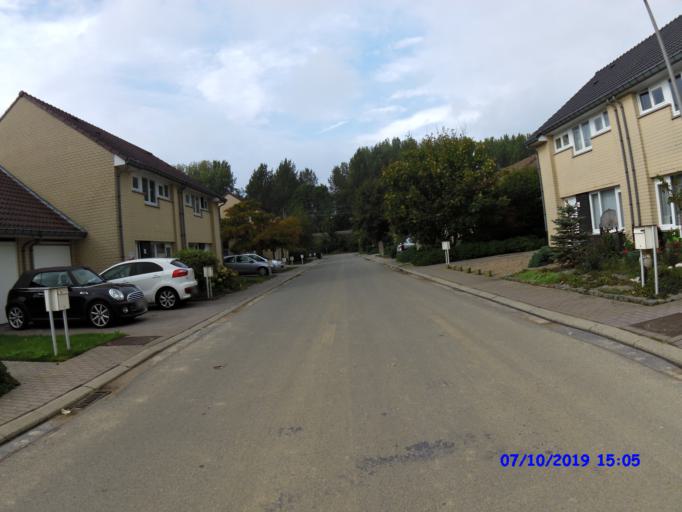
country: BE
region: Flanders
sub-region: Provincie Oost-Vlaanderen
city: Zottegem
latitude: 50.8763
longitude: 3.8210
